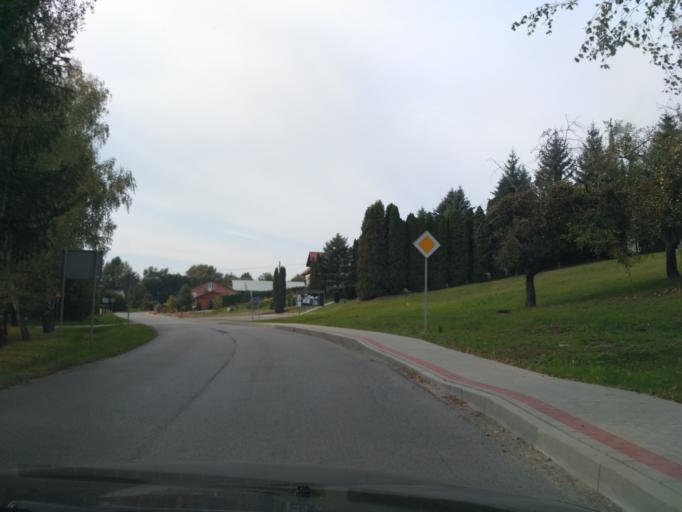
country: PL
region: Subcarpathian Voivodeship
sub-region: Powiat rzeszowski
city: Zglobien
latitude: 50.0375
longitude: 21.8387
